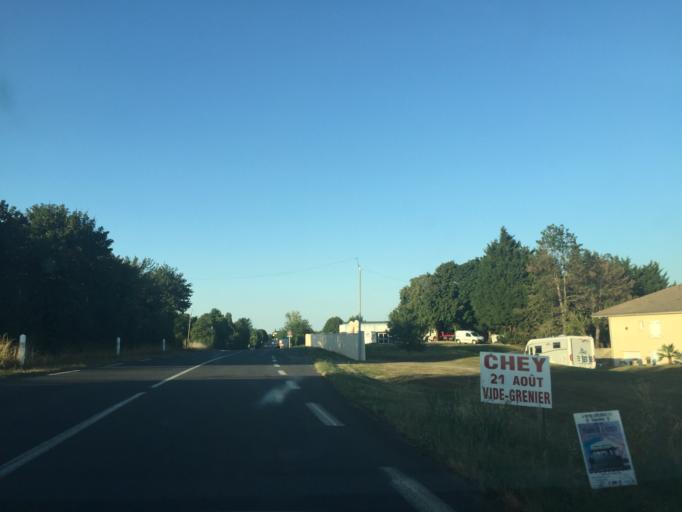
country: FR
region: Poitou-Charentes
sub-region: Departement des Deux-Sevres
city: Lezay
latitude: 46.2973
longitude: -0.0614
